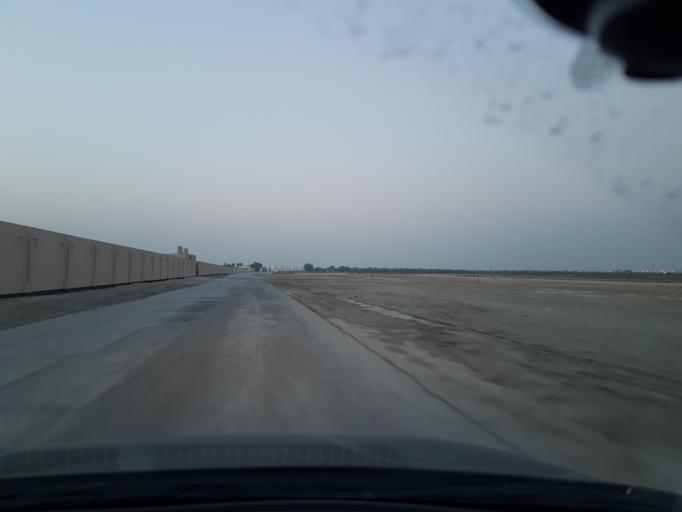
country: BH
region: Central Governorate
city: Dar Kulayb
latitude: 26.0063
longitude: 50.4747
